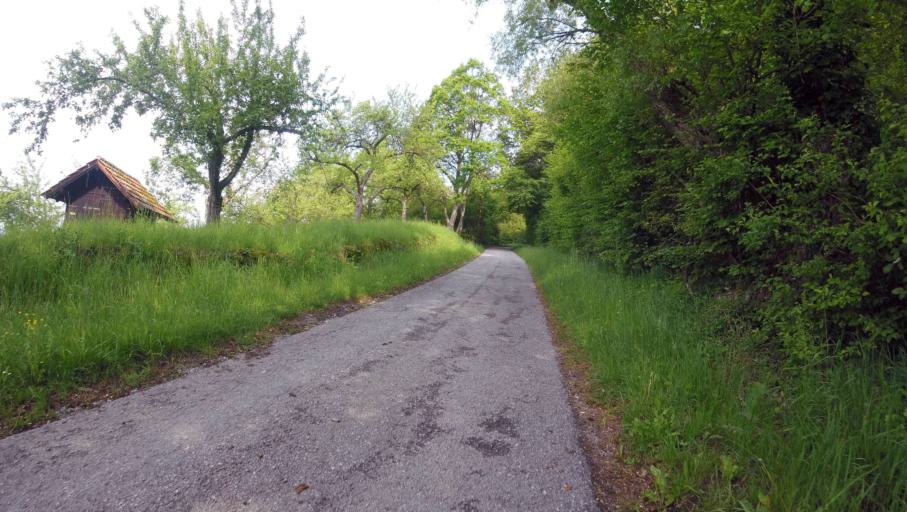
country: DE
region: Baden-Wuerttemberg
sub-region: Regierungsbezirk Stuttgart
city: Althutte
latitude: 48.9342
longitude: 9.5352
